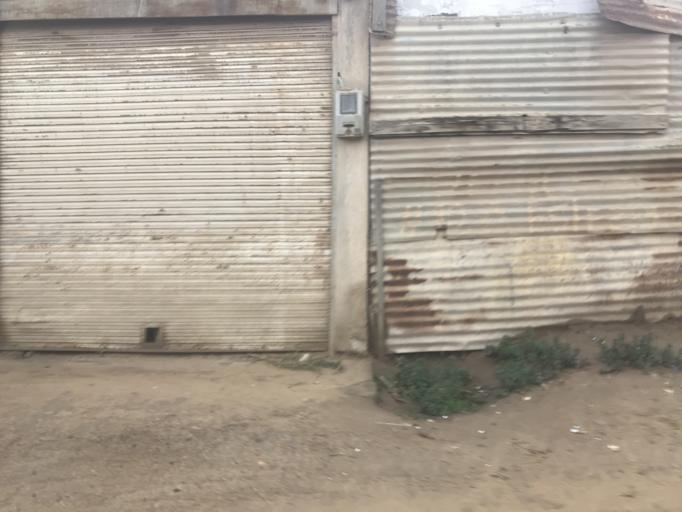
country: CO
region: Cundinamarca
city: Soacha
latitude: 4.5641
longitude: -74.2187
